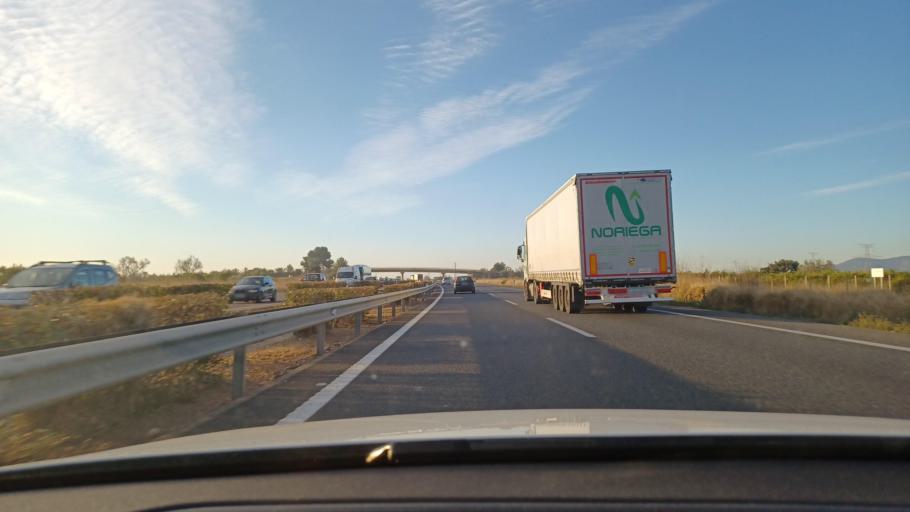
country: ES
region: Valencia
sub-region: Provincia de Castello
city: Alquerias del Nino Perdido
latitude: 39.9277
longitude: -0.1362
